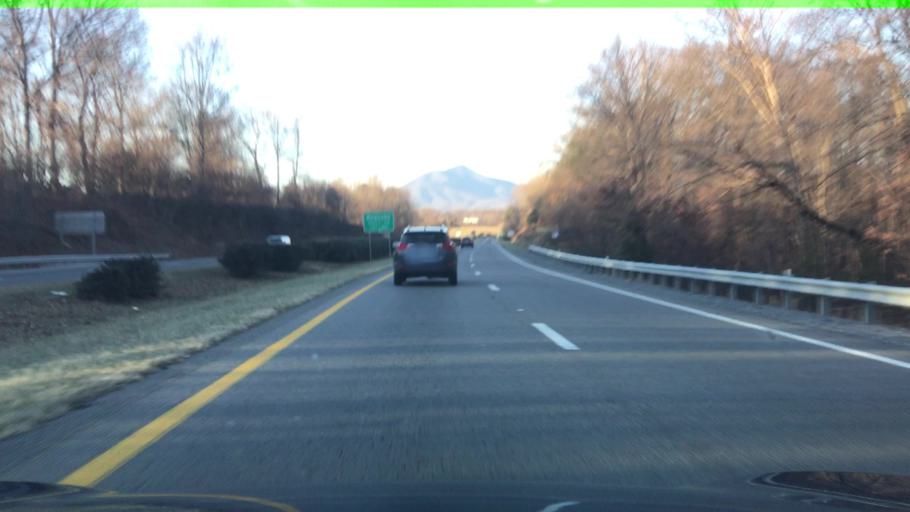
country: US
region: Virginia
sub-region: City of Bedford
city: Bedford
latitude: 37.3283
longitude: -79.5403
